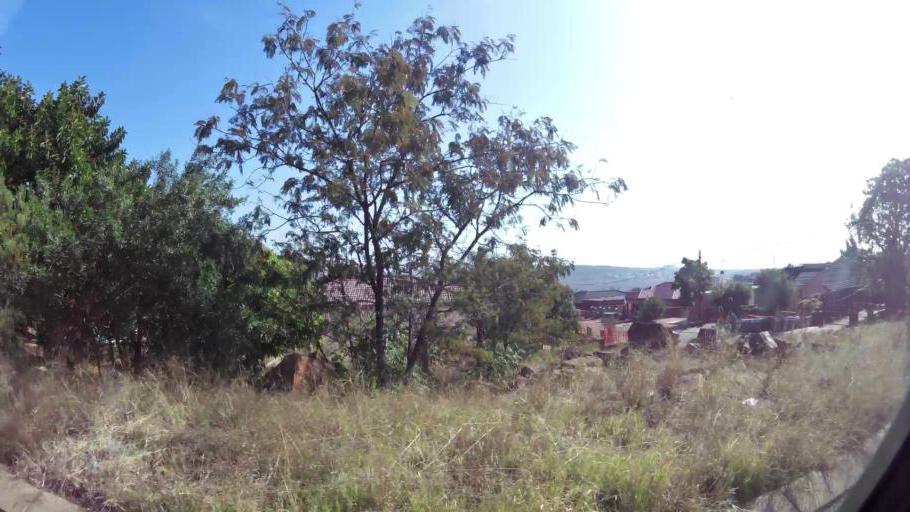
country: ZA
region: Gauteng
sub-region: City of Tshwane Metropolitan Municipality
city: Mabopane
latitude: -25.5319
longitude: 28.0915
